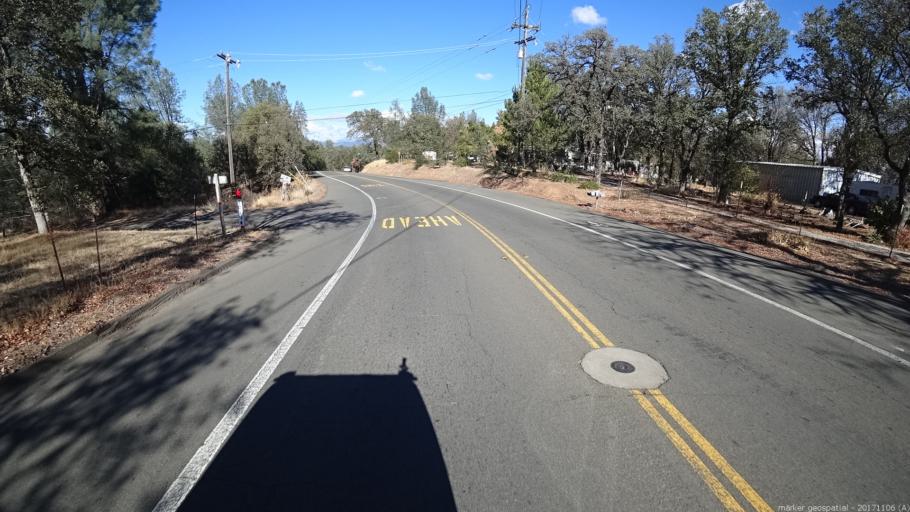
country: US
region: California
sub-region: Shasta County
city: Palo Cedro
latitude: 40.5841
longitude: -122.3070
